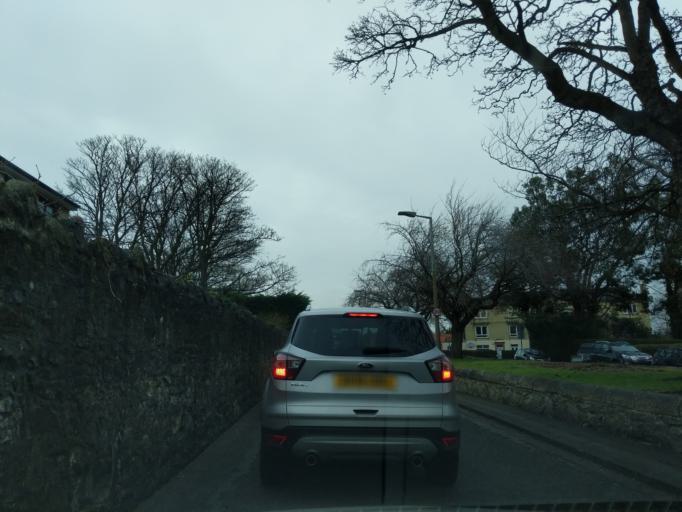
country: GB
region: Scotland
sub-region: Edinburgh
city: Edinburgh
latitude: 55.9718
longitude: -3.1992
